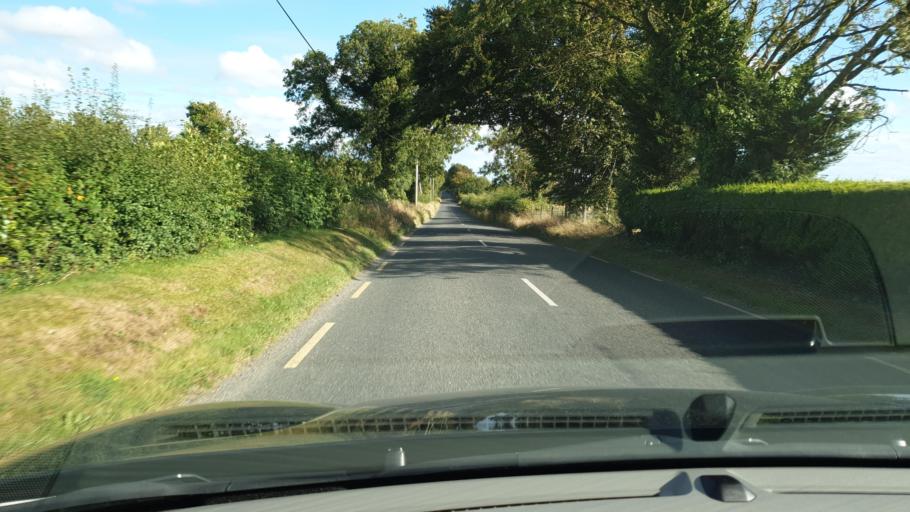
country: IE
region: Leinster
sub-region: An Mhi
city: Ashbourne
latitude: 53.4706
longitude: -6.4201
